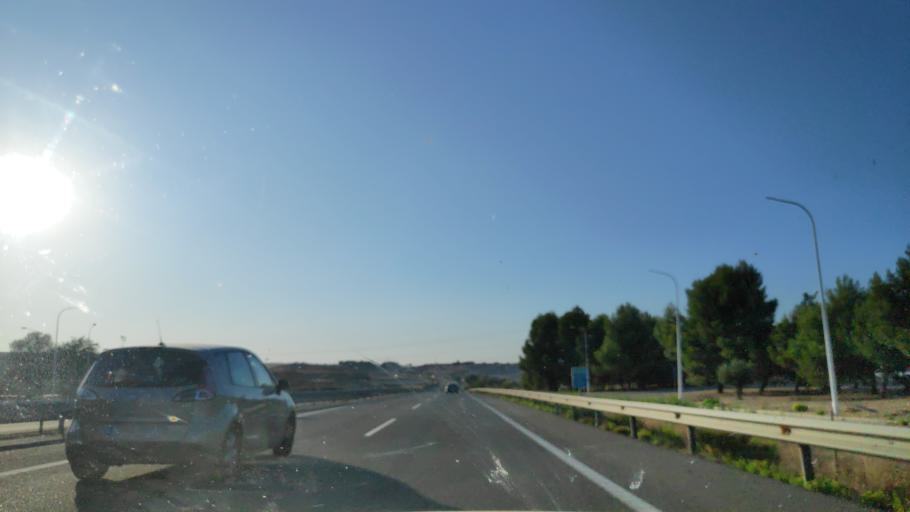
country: ES
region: Castille-La Mancha
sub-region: Provincia de Cuenca
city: Belinchon
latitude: 40.0325
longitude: -3.0415
